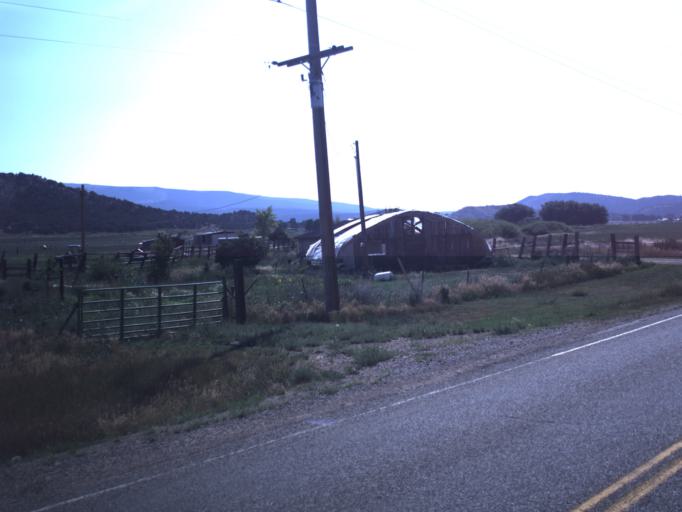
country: US
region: Utah
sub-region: Duchesne County
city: Duchesne
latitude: 40.3827
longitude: -110.7402
